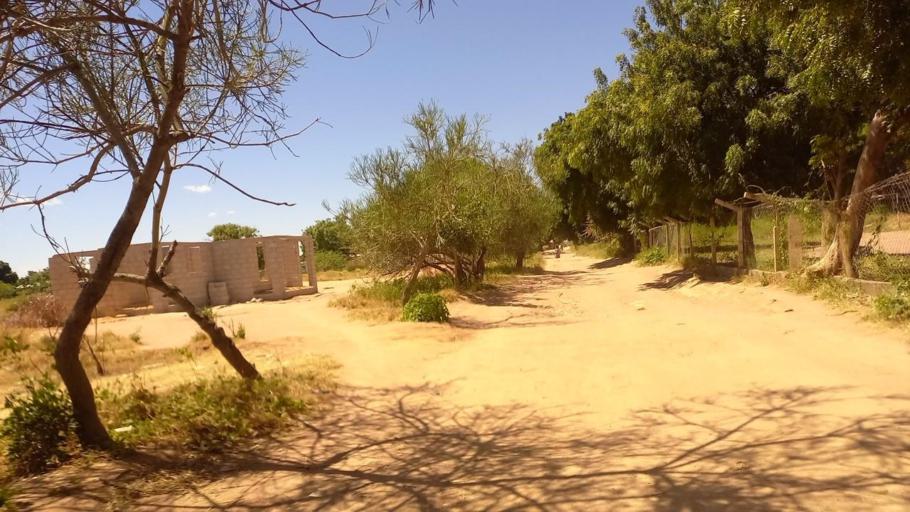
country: TZ
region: Dodoma
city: Dodoma
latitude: -6.1209
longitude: 35.7427
